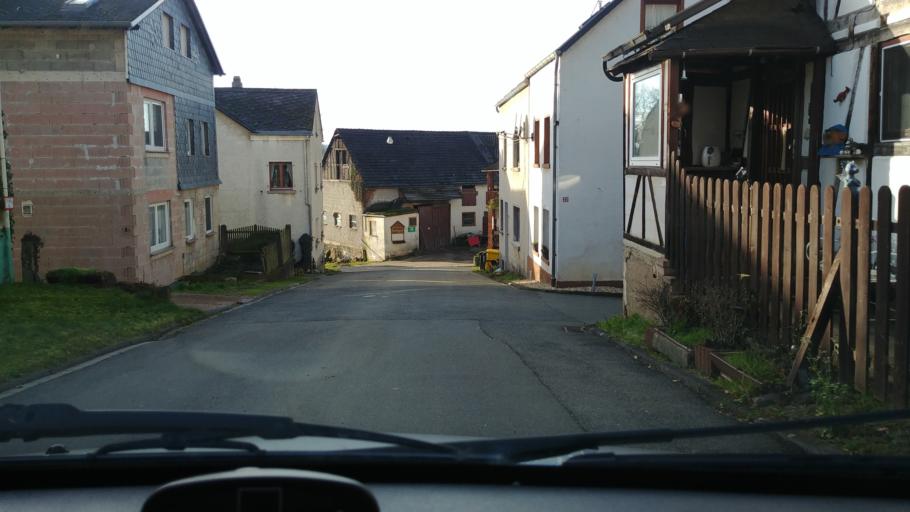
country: DE
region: Rheinland-Pfalz
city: Attenhausen
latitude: 50.2909
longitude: 7.8736
